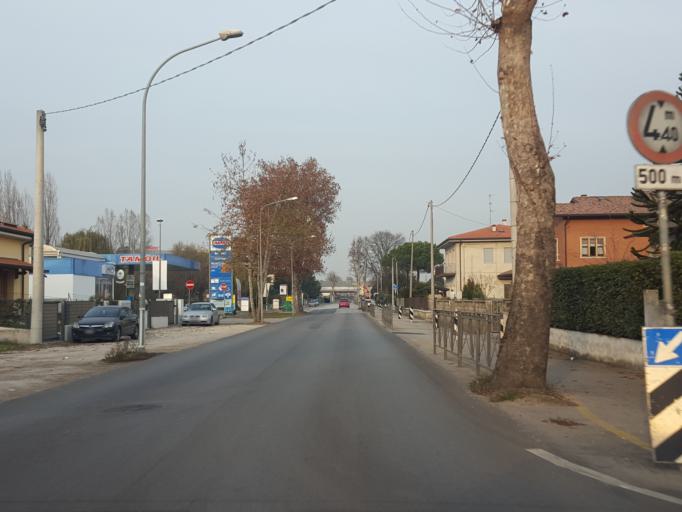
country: IT
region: Veneto
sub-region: Provincia di Vicenza
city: Creazzo
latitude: 45.5152
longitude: 11.5097
